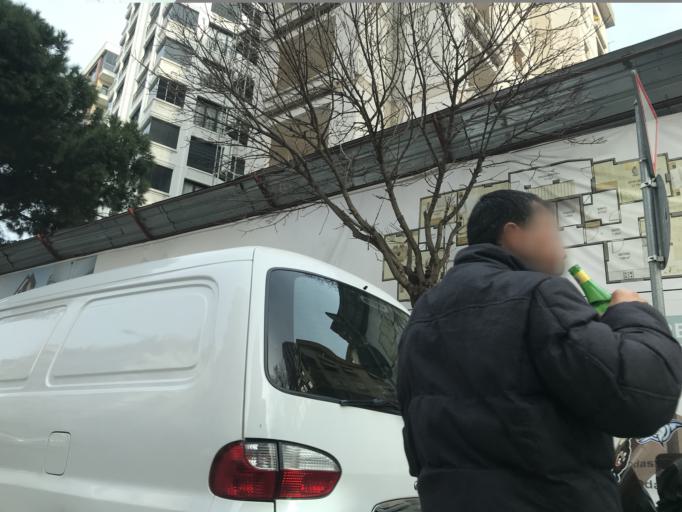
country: TR
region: Istanbul
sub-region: Atasehir
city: Atasehir
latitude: 40.9623
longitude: 29.0965
